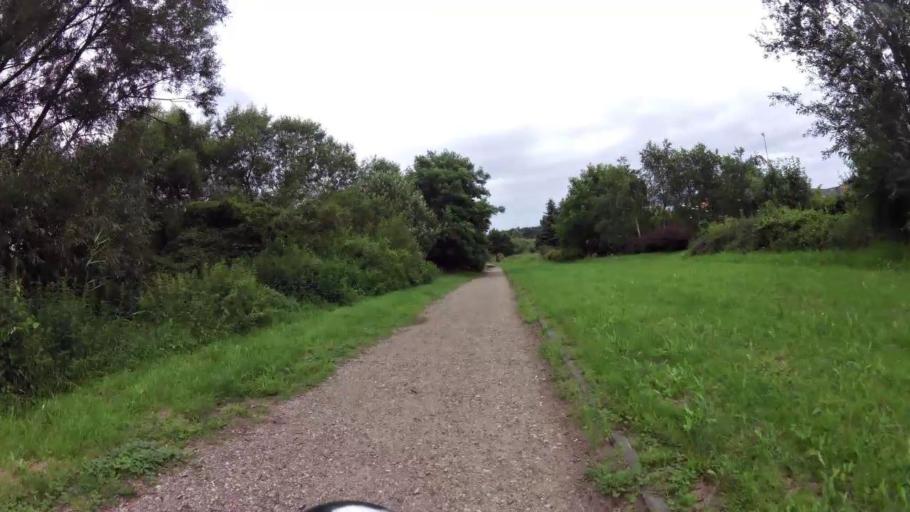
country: PL
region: West Pomeranian Voivodeship
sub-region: Powiat bialogardzki
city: Karlino
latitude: 54.0438
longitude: 15.8697
